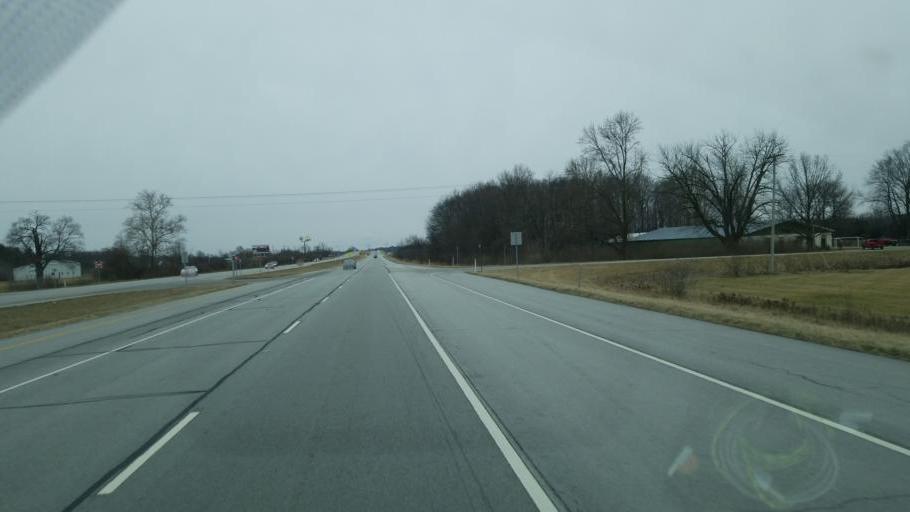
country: US
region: Indiana
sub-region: Marshall County
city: Argos
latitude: 41.2451
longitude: -86.2617
